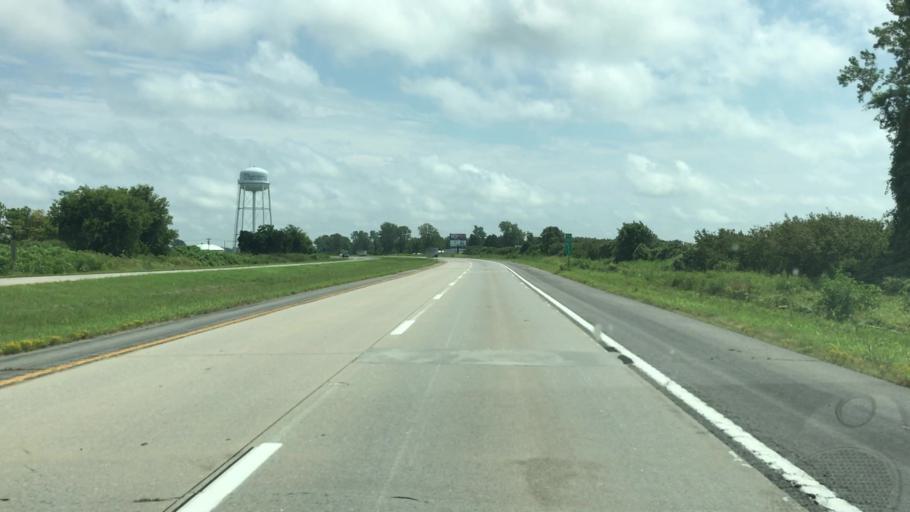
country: US
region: Missouri
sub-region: Pemiscot County
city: Caruthersville
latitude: 36.1586
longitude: -89.6759
